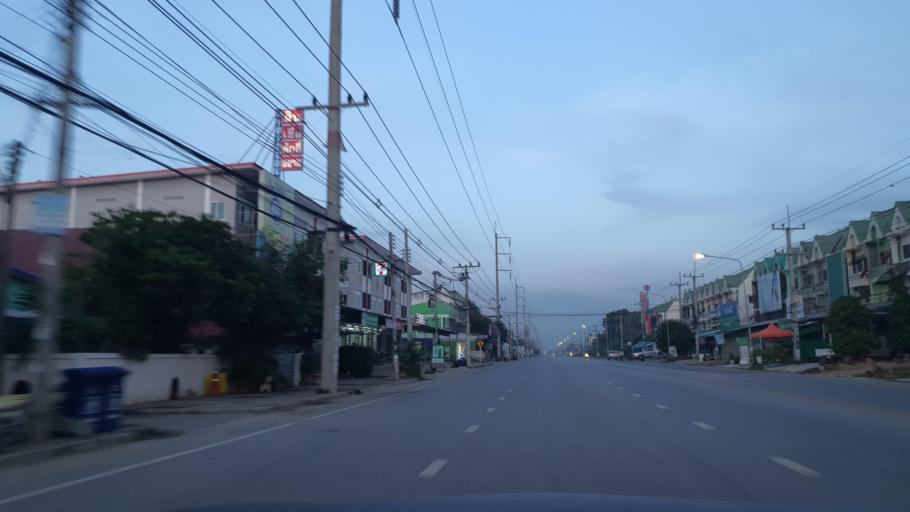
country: TH
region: Nakhon Sawan
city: Kao Liao
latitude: 15.7668
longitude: 99.9850
